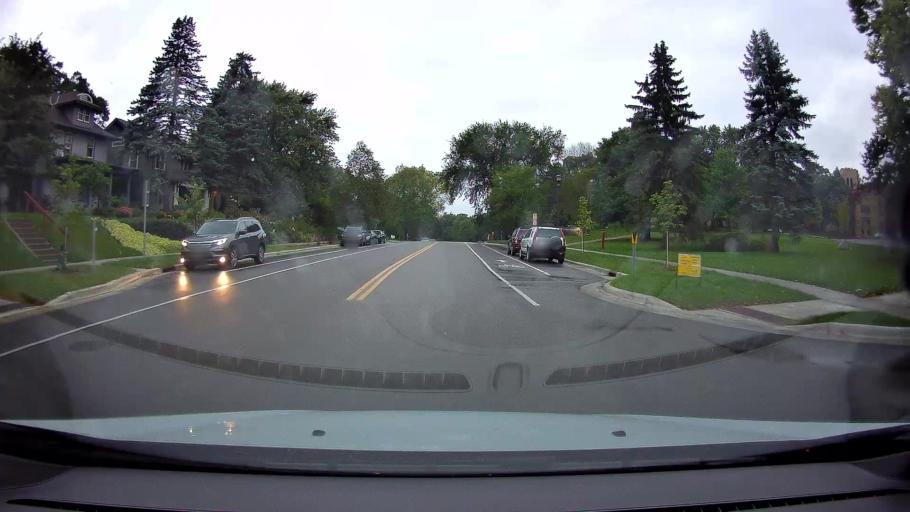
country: US
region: Minnesota
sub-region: Ramsey County
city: Lauderdale
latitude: 44.9828
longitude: -93.1963
